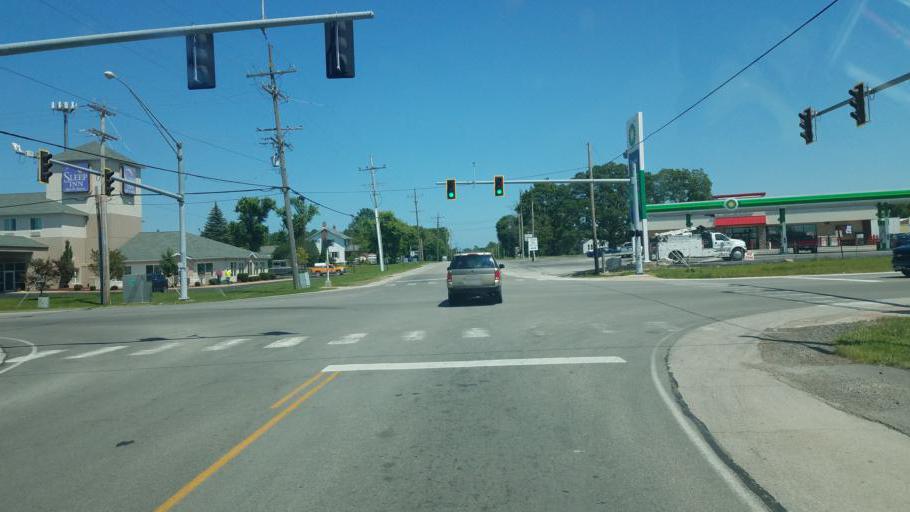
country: US
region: Ohio
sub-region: Ottawa County
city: Port Clinton
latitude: 41.5083
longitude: -82.8598
